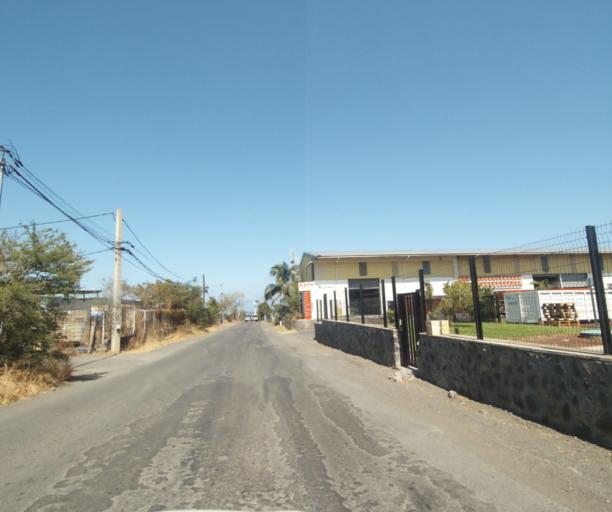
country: RE
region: Reunion
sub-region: Reunion
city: Le Port
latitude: -20.9628
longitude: 55.2929
